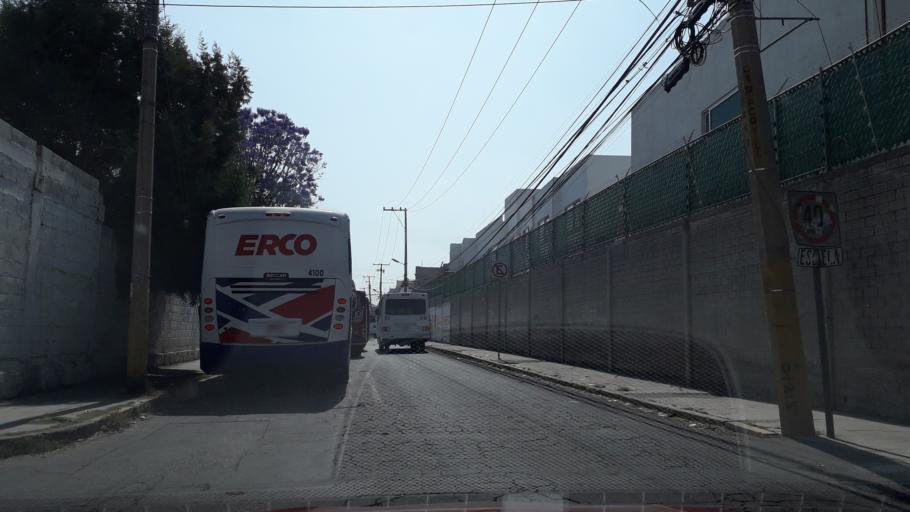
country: MX
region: Puebla
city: Puebla
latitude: 19.0770
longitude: -98.2153
